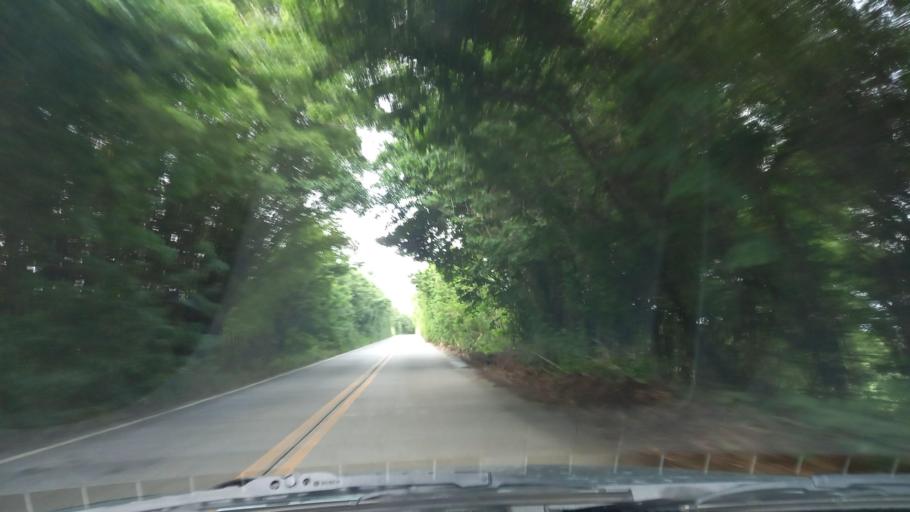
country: BR
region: Pernambuco
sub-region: Quipapa
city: Quipapa
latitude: -8.7858
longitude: -35.9564
